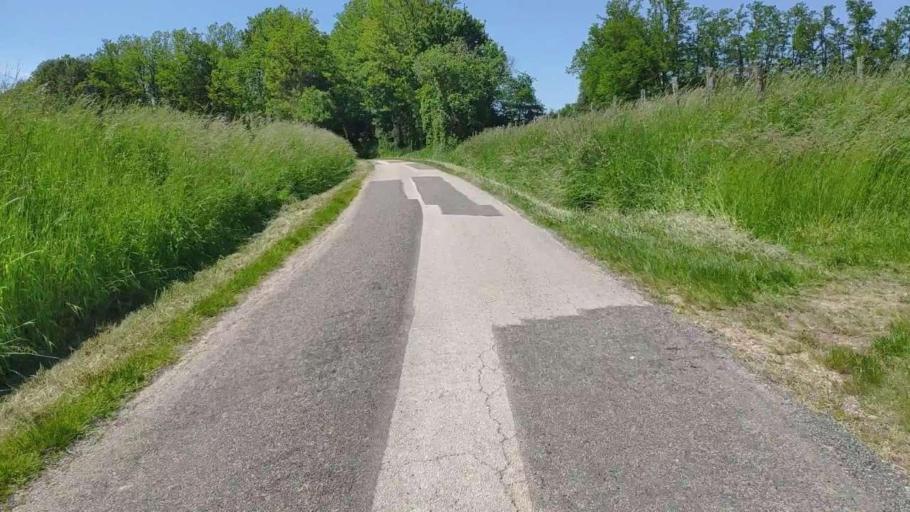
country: FR
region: Franche-Comte
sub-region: Departement du Jura
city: Bletterans
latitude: 46.7474
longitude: 5.3986
